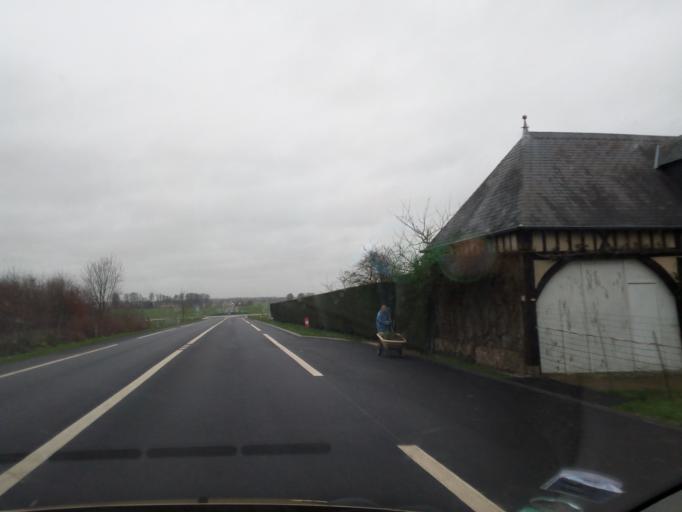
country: FR
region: Haute-Normandie
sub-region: Departement de la Seine-Maritime
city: Auzebosc
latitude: 49.5841
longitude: 0.7320
